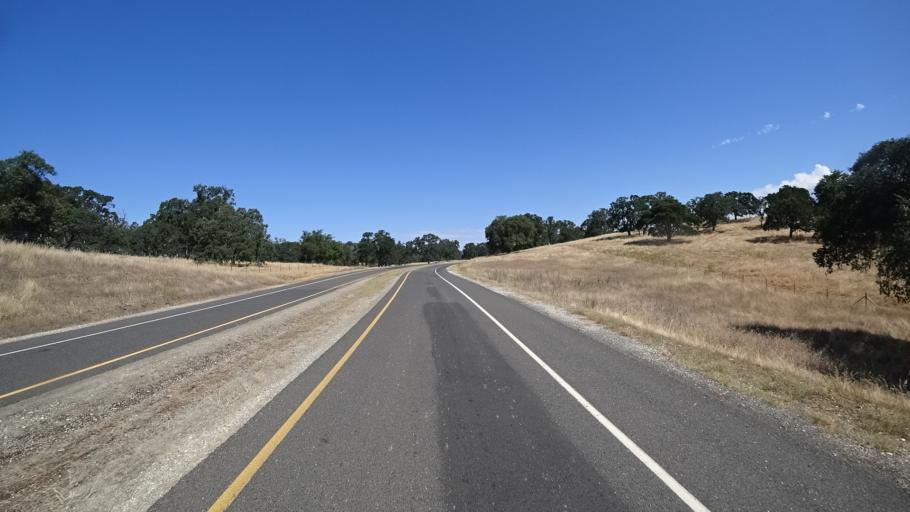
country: US
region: California
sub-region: Calaveras County
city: Copperopolis
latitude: 37.9484
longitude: -120.6516
